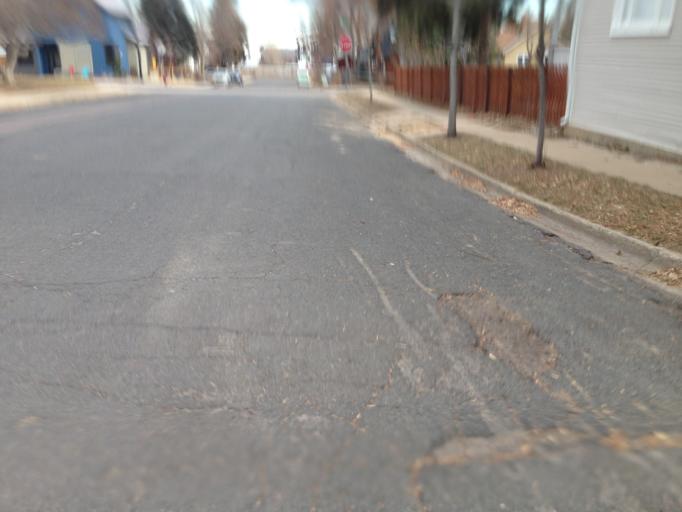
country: US
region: Colorado
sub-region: Boulder County
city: Louisville
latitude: 39.9807
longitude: -105.1331
